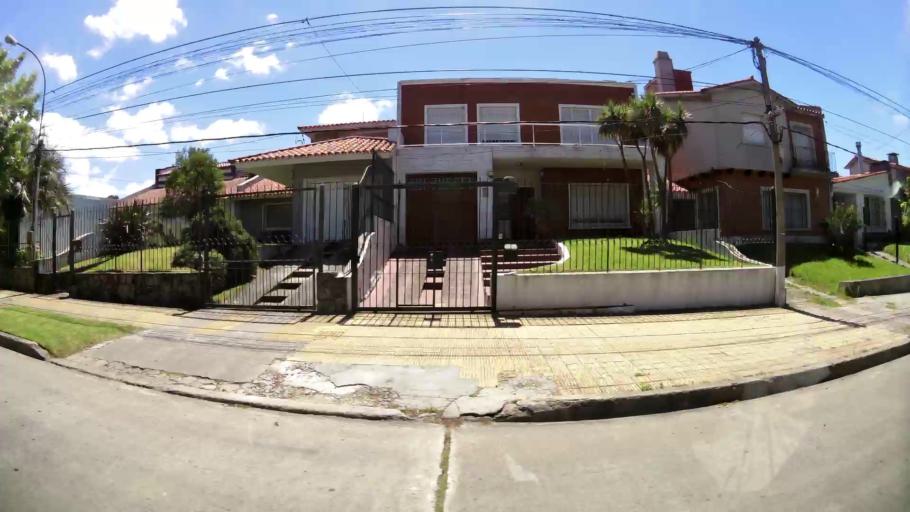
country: UY
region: Canelones
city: Paso de Carrasco
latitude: -34.8878
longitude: -56.0973
